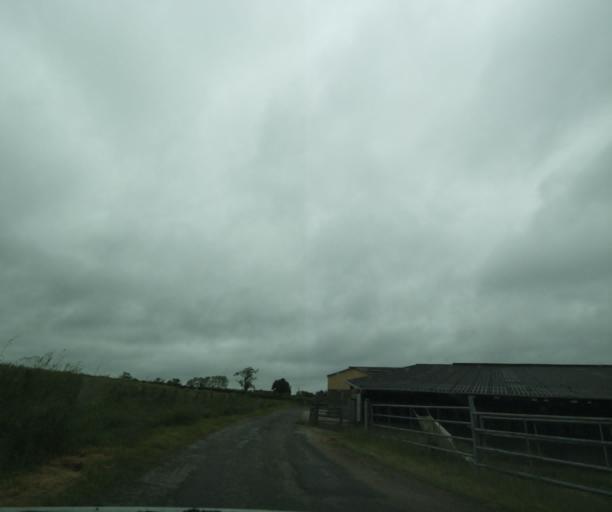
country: FR
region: Bourgogne
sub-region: Departement de Saone-et-Loire
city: Palinges
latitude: 46.5618
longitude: 4.2036
